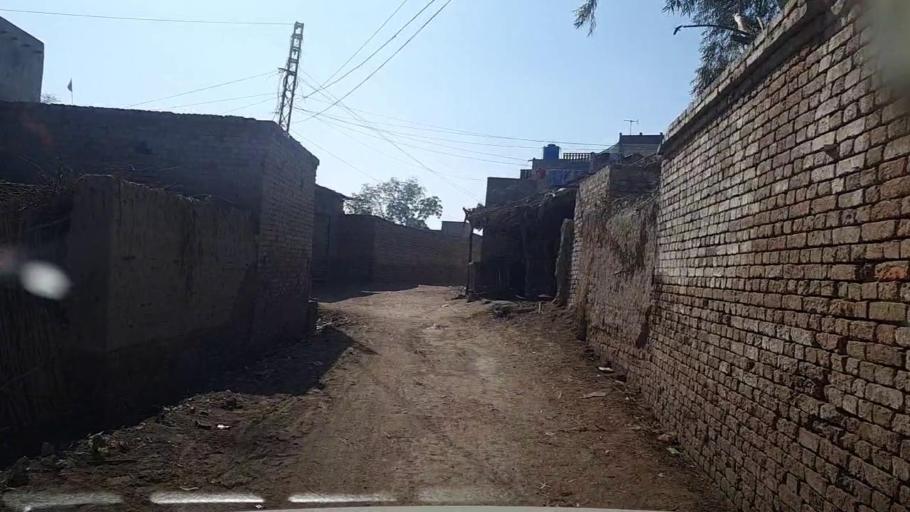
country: PK
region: Sindh
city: Khairpur
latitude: 27.9569
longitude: 69.6862
